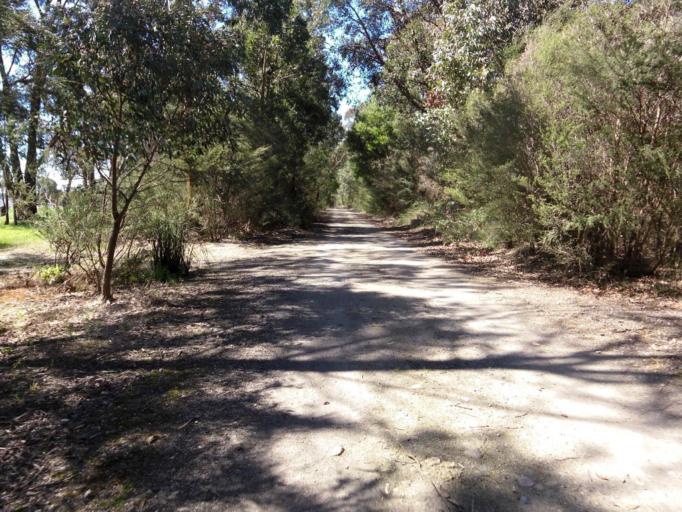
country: AU
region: Victoria
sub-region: Latrobe
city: Moe
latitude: -38.1718
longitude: 146.2939
